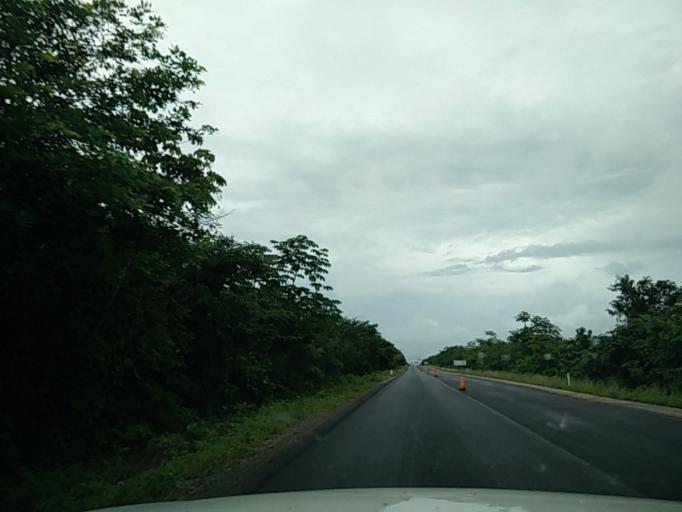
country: MX
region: Quintana Roo
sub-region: Lazaro Cardenas
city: El Tintal
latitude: 20.9010
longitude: -87.4628
